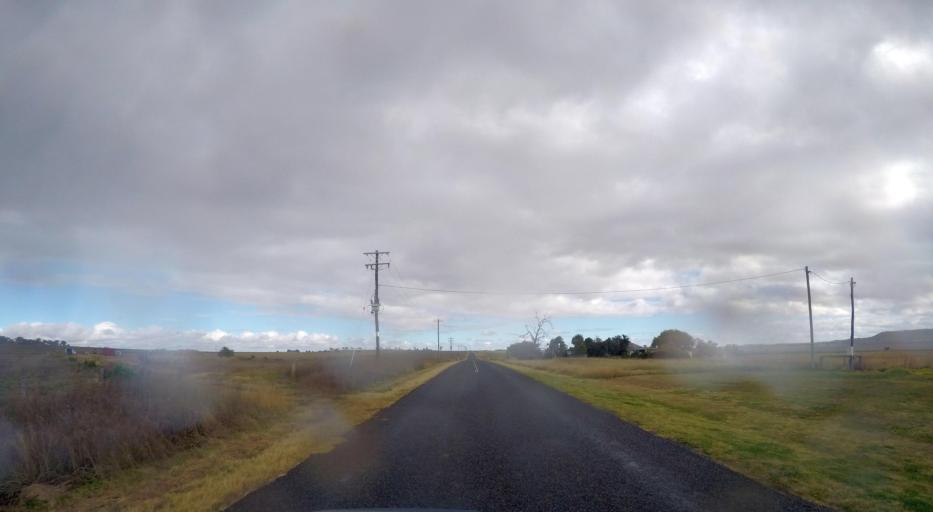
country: AU
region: Queensland
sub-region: Southern Downs
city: Warwick
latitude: -28.0514
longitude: 152.0334
